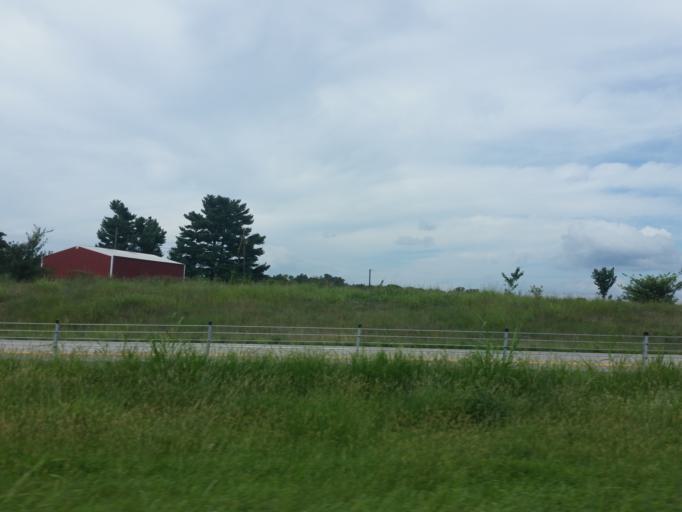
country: US
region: Kentucky
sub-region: Trigg County
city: Cadiz
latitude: 36.9206
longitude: -87.7979
